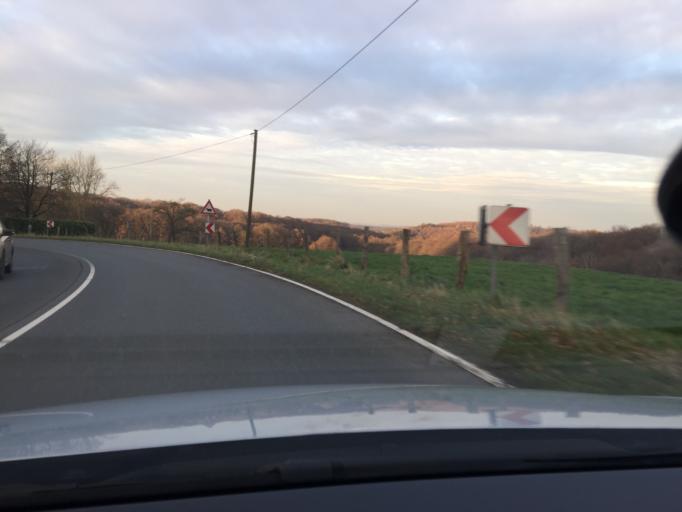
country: DE
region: North Rhine-Westphalia
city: Sprockhovel
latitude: 51.3226
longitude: 7.2485
